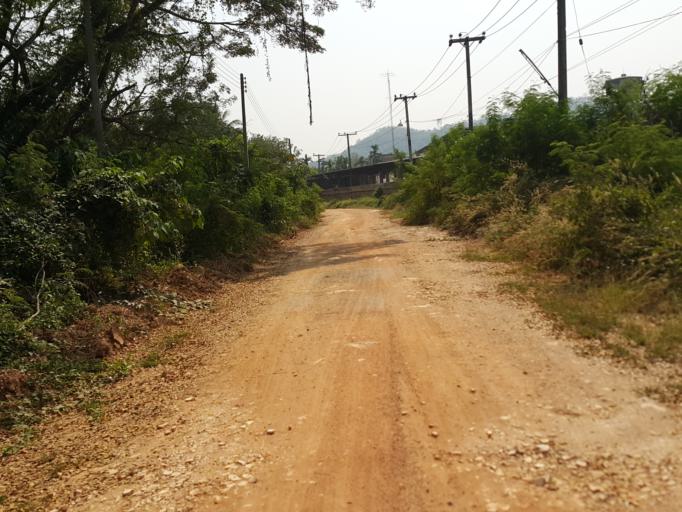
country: TH
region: Sukhothai
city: Thung Saliam
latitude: 17.3327
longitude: 99.4922
